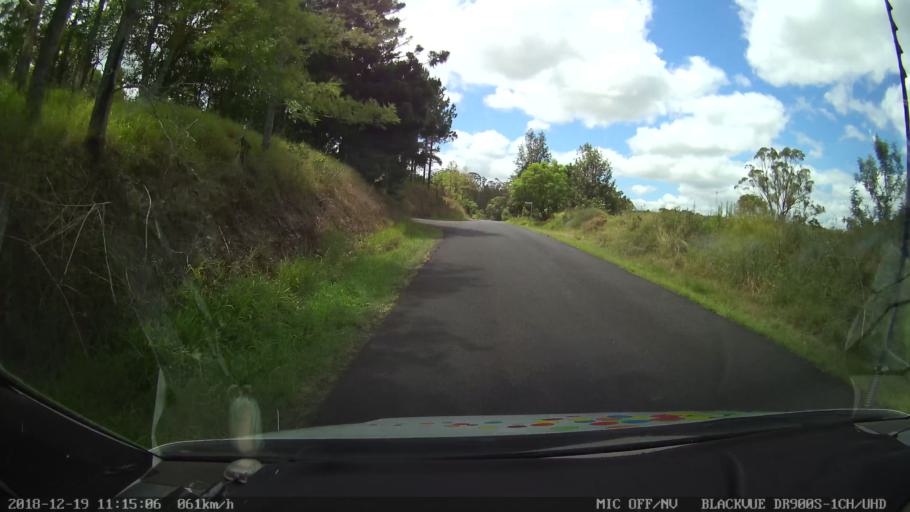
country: AU
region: New South Wales
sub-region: Lismore Municipality
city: Nimbin
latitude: -28.6653
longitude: 153.2762
